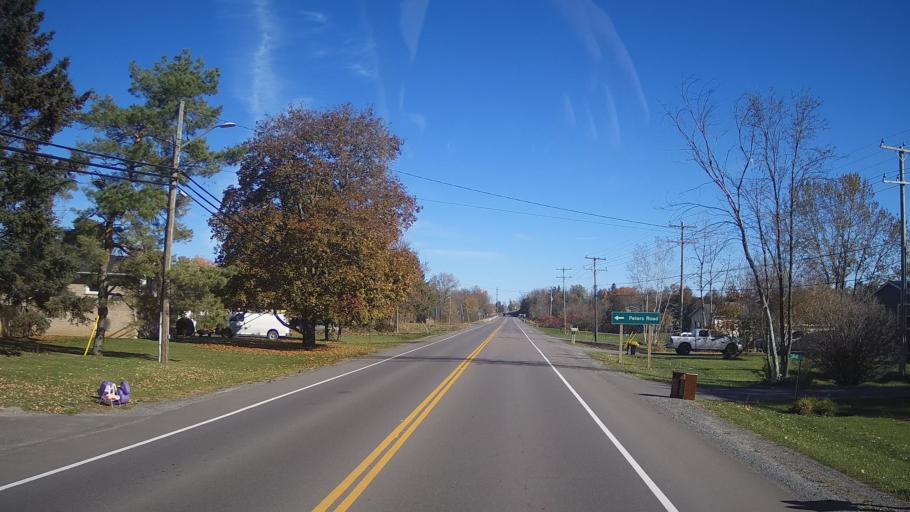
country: CA
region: Ontario
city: Kingston
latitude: 44.4059
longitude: -76.6571
